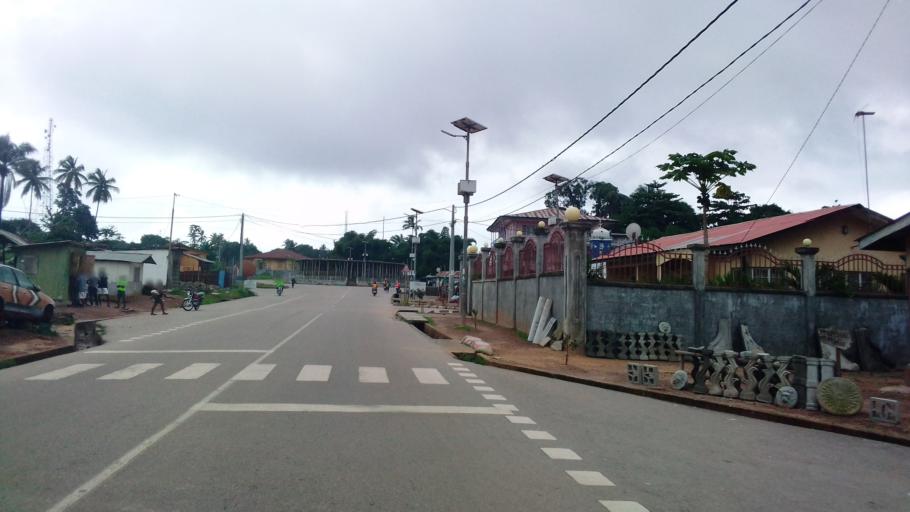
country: SL
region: Northern Province
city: Lunsar
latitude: 8.6861
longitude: -12.5356
